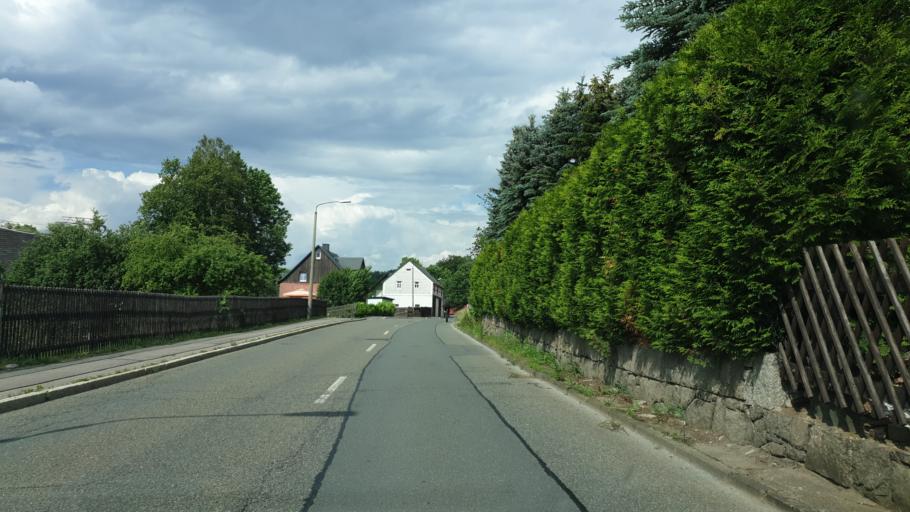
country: DE
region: Saxony
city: Aue
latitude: 50.6091
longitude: 12.7052
